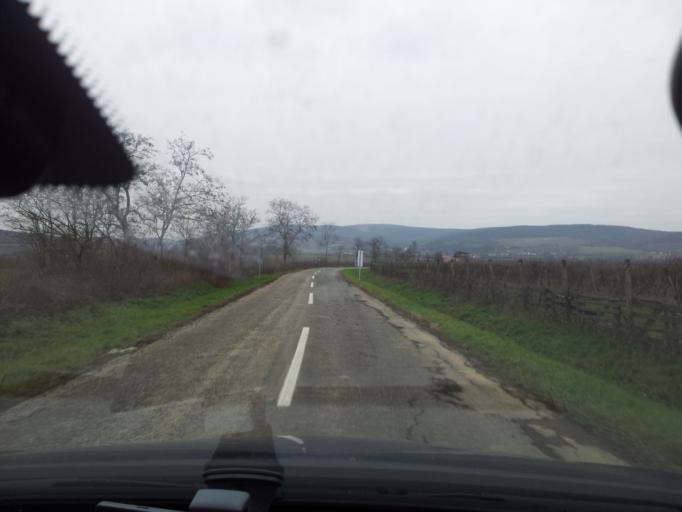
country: HU
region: Borsod-Abauj-Zemplen
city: Satoraljaujhely
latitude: 48.4462
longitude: 21.6565
